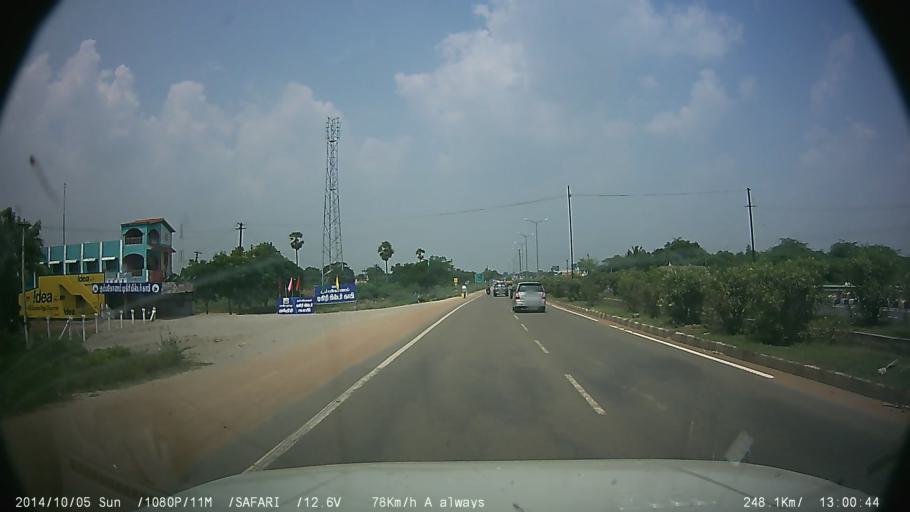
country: IN
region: Tamil Nadu
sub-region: Villupuram
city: Villupuram
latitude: 11.8311
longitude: 79.4262
